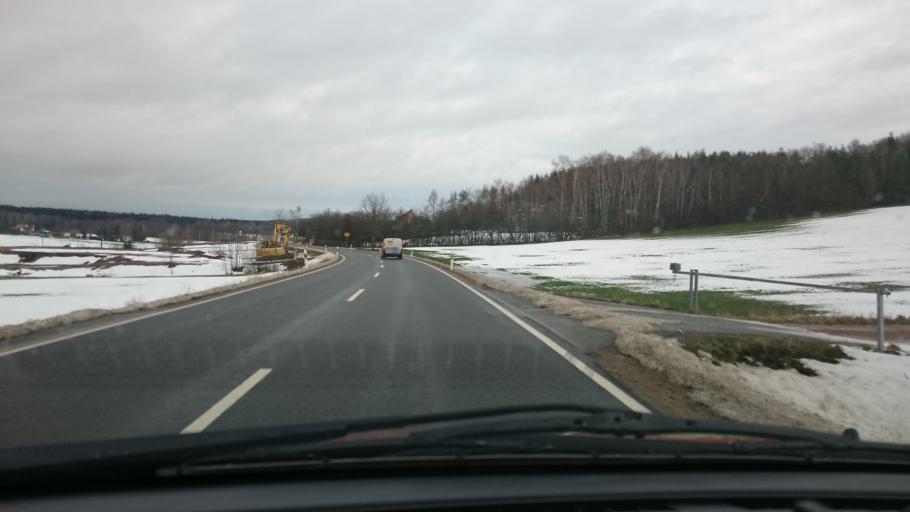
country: DE
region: Saxony
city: Waldkirchen
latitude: 50.6043
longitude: 12.4159
